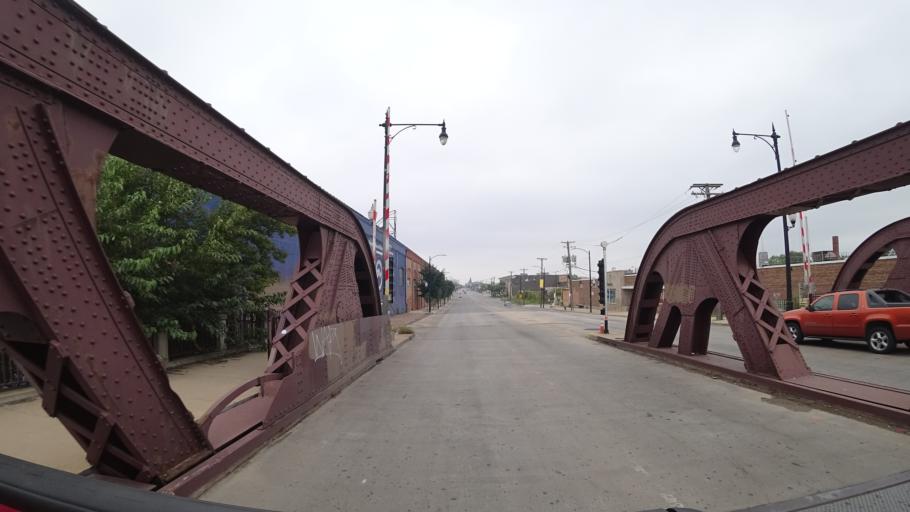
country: US
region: Illinois
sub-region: Cook County
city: Chicago
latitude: 41.8452
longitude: -87.6660
